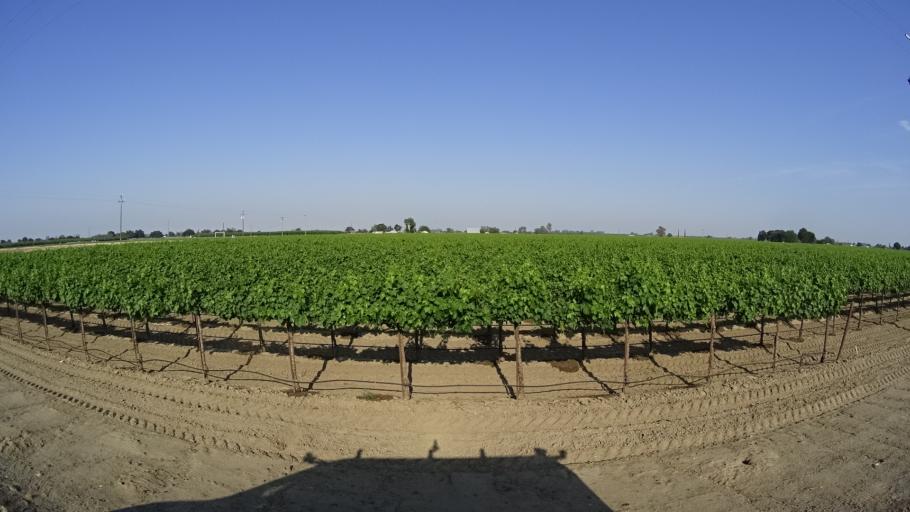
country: US
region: California
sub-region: Fresno County
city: Riverdale
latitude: 36.3664
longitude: -119.8430
